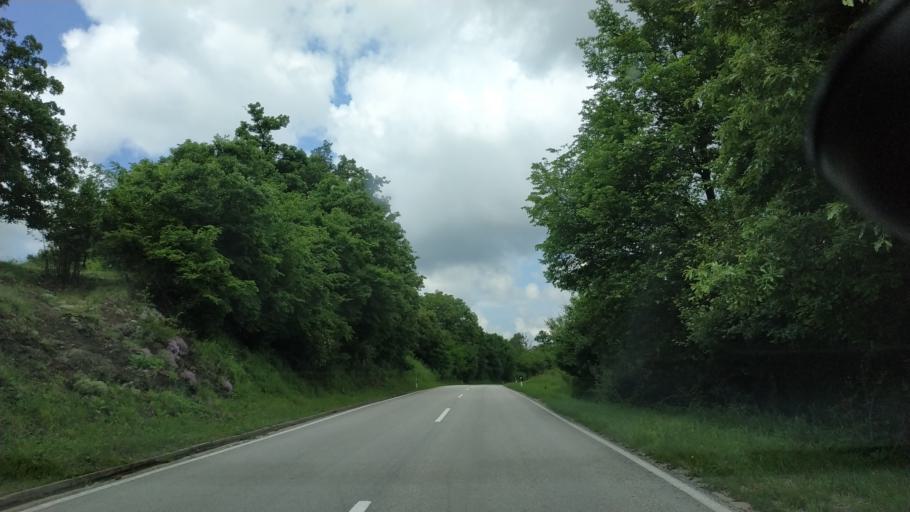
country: RS
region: Central Serbia
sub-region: Borski Okrug
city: Bor
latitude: 44.0754
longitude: 22.0254
